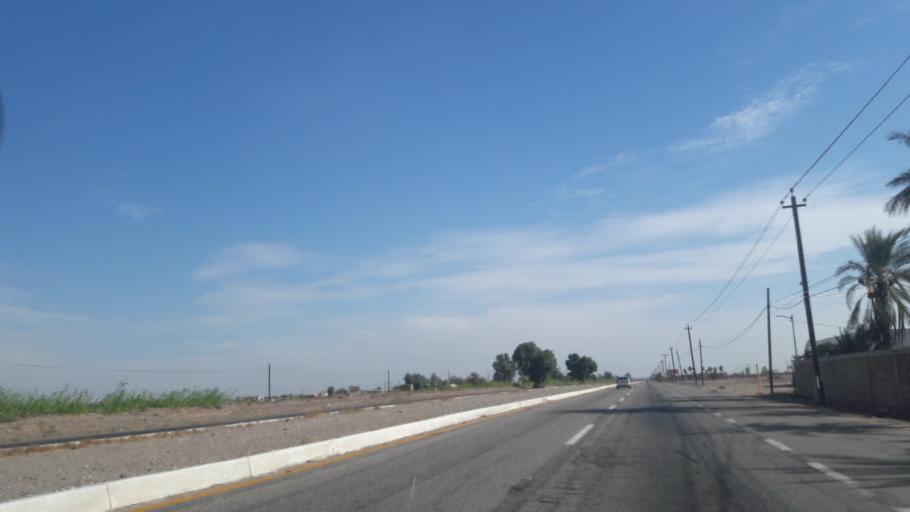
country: MX
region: Baja California
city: Progreso
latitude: 32.5932
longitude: -115.6249
